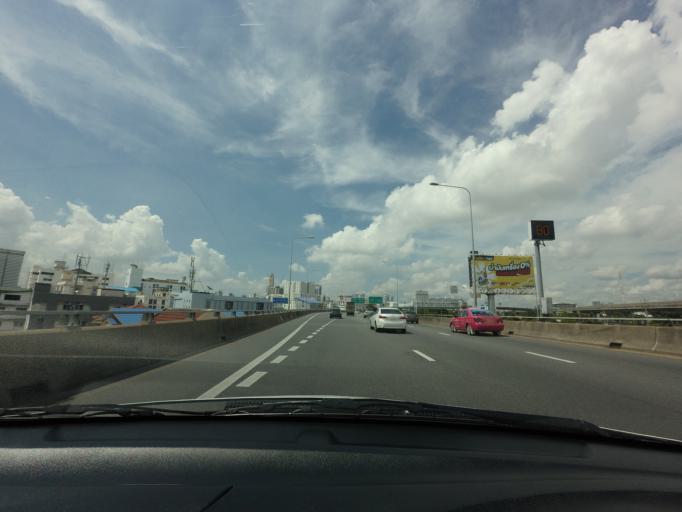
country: TH
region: Bangkok
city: Phaya Thai
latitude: 13.7762
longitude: 100.5328
